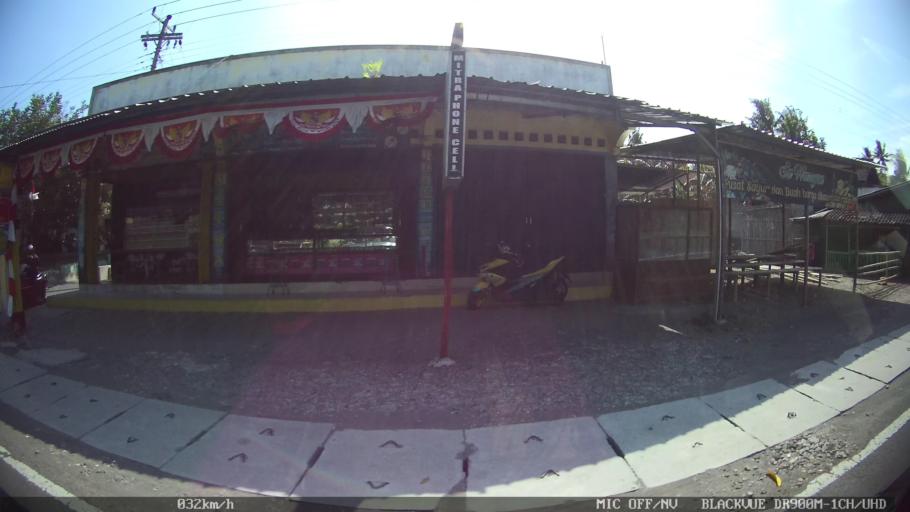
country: ID
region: Daerah Istimewa Yogyakarta
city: Pundong
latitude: -7.9857
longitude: 110.3157
